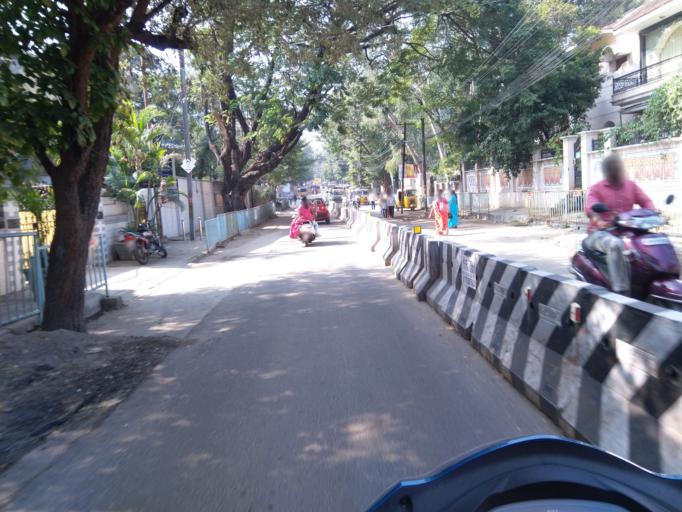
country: IN
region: Telangana
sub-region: Rangareddi
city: Kukatpalli
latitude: 17.4312
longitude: 78.4067
